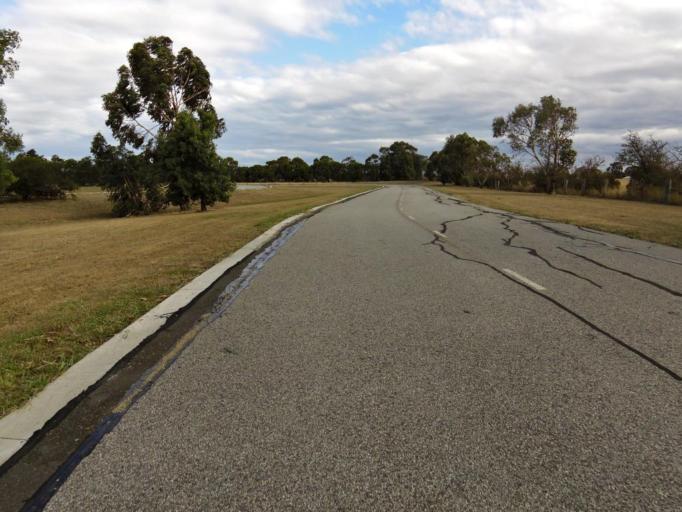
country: AU
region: Victoria
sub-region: Casey
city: Cranbourne East
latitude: -38.1266
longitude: 145.3111
